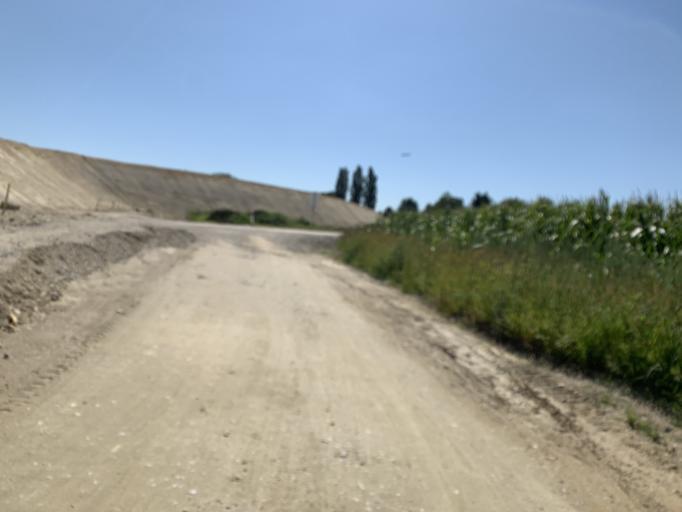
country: DE
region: Bavaria
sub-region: Upper Bavaria
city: Freising
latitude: 48.3847
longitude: 11.7262
